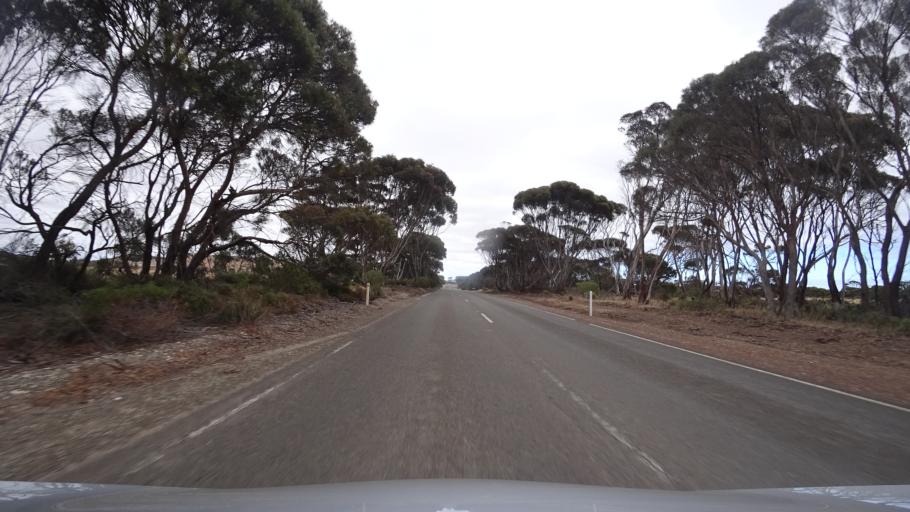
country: AU
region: South Australia
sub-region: Kangaroo Island
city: Kingscote
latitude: -35.6266
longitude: 137.5456
